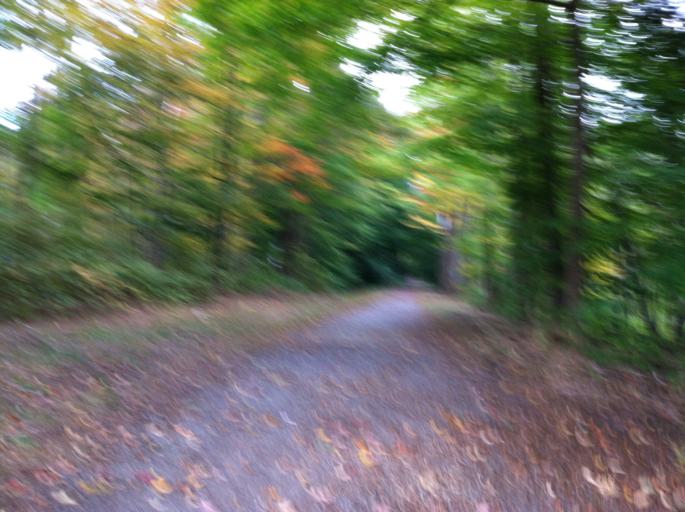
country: US
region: Massachusetts
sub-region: Middlesex County
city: Bedford
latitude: 42.4908
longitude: -71.2762
